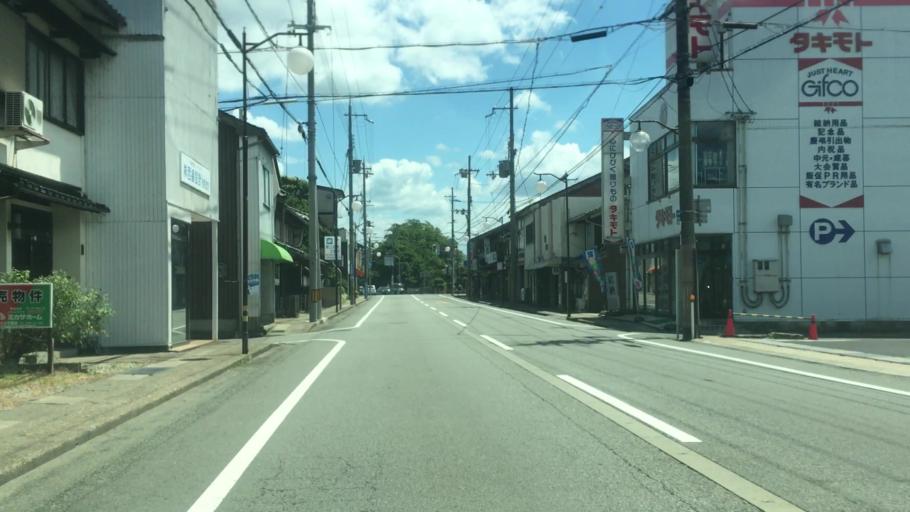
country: JP
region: Hyogo
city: Toyooka
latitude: 35.5366
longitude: 134.8252
